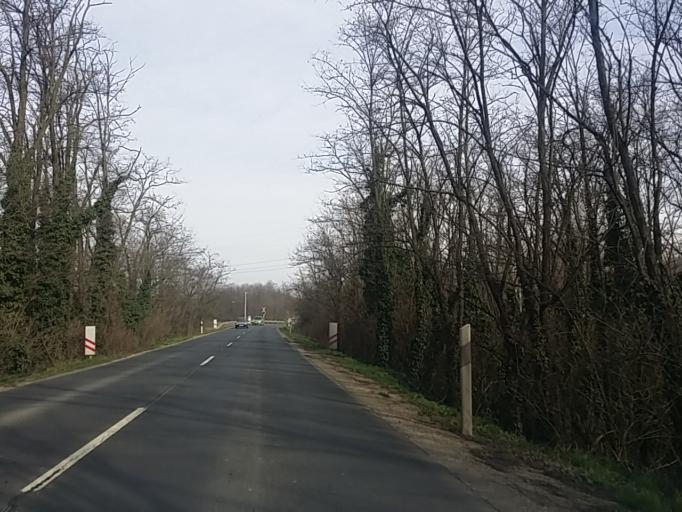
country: HU
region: Pest
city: Fot
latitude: 47.6267
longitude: 19.1989
